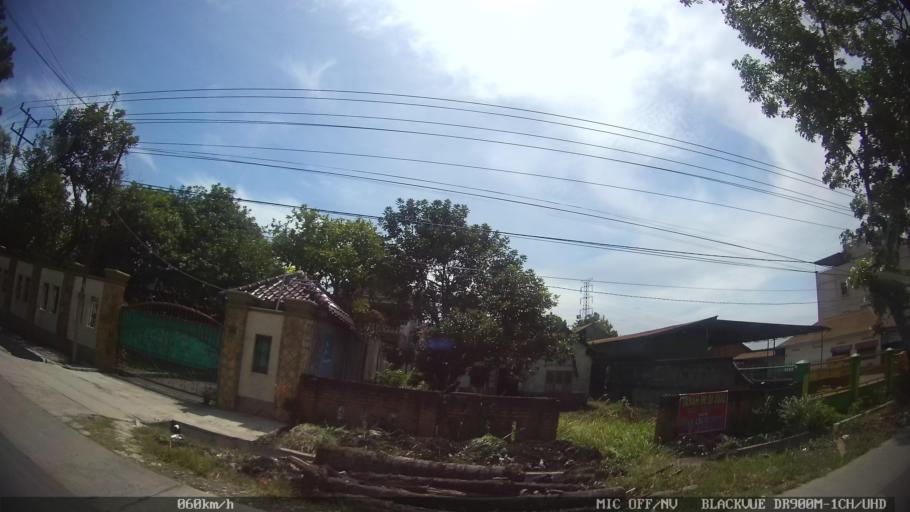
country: ID
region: North Sumatra
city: Binjai
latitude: 3.6419
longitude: 98.5104
